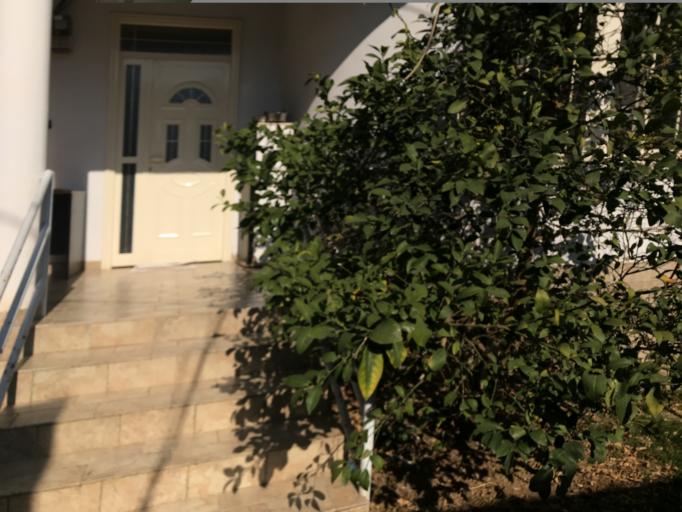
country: AL
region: Tirane
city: Tirana
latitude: 41.3363
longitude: 19.8323
